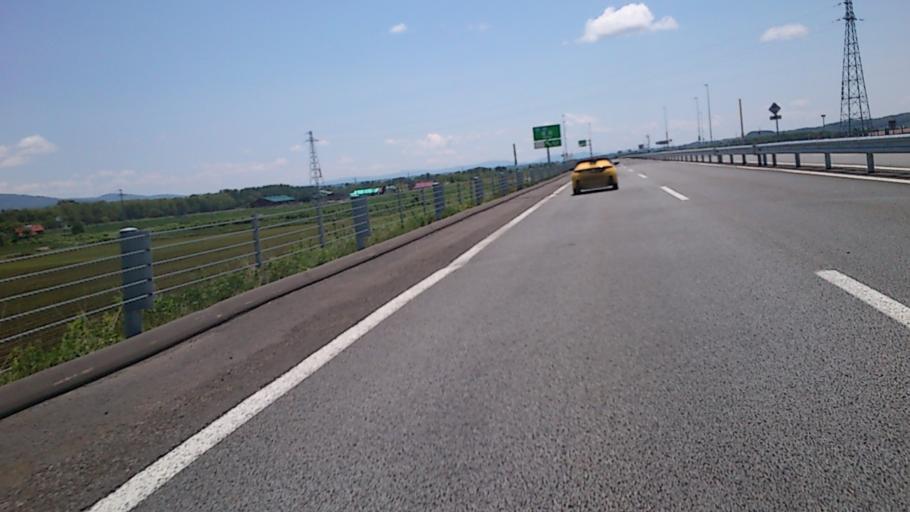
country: JP
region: Hokkaido
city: Nayoro
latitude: 44.4793
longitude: 142.3681
